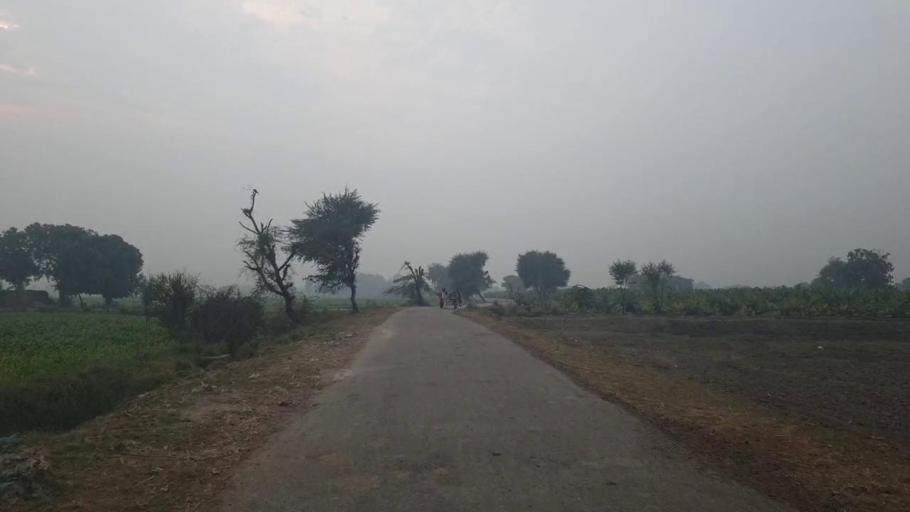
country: PK
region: Sindh
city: Tando Adam
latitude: 25.7370
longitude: 68.6695
